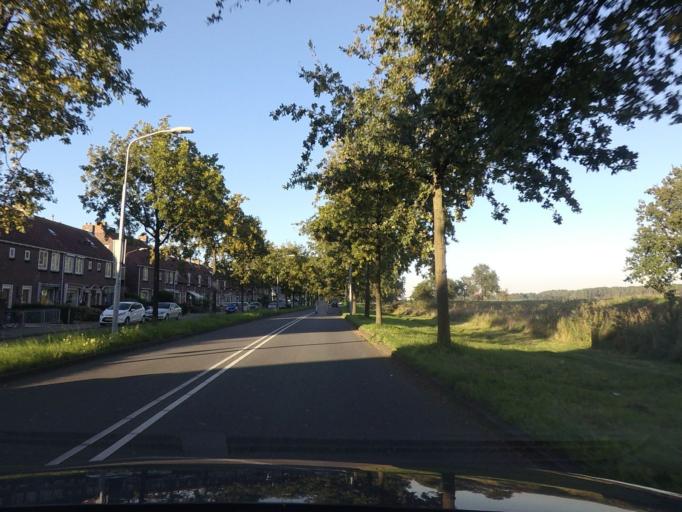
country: NL
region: North Holland
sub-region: Gemeente Bloemendaal
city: Bloemendaal
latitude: 52.4152
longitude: 4.6576
